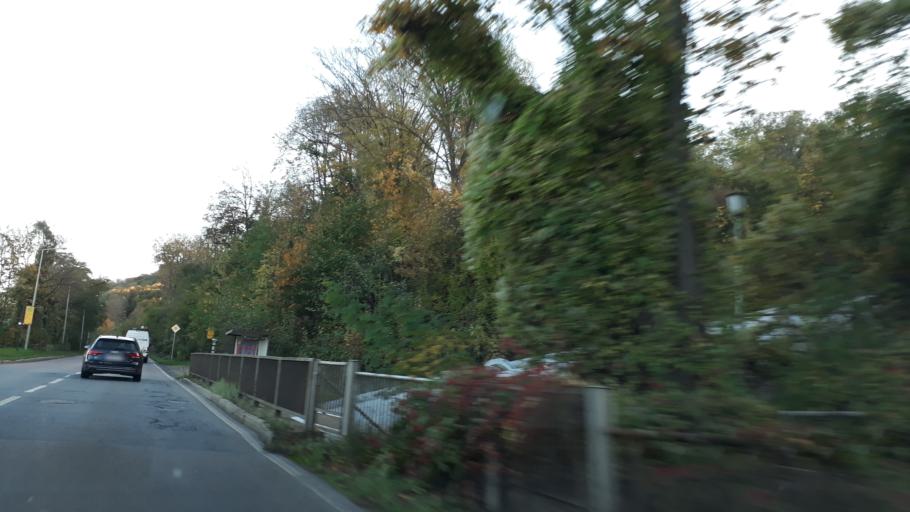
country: DE
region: Saxony
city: Coswig
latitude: 51.0909
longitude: 13.6084
